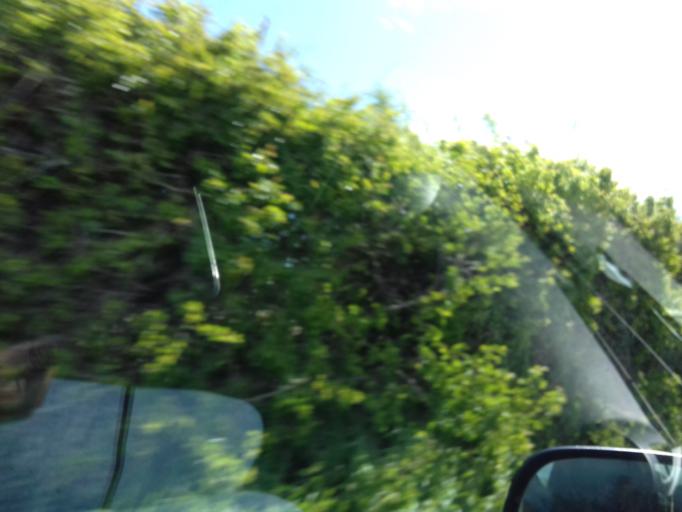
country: IE
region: Munster
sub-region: Waterford
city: Dunmore East
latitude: 52.2420
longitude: -6.8581
